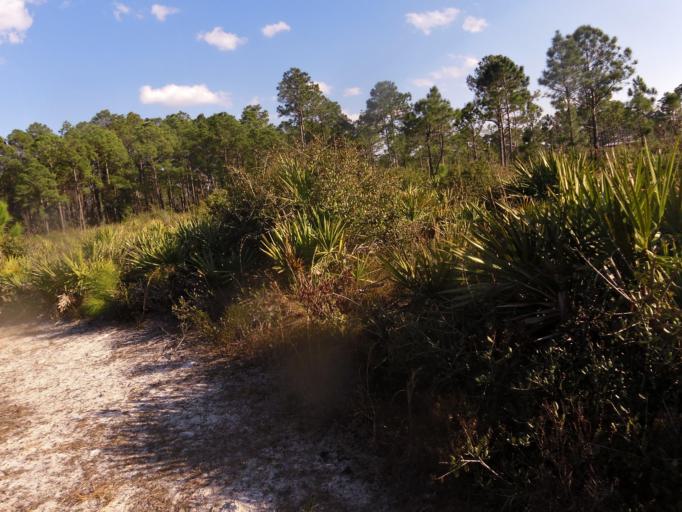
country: US
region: Florida
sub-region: Duval County
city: Atlantic Beach
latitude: 30.4747
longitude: -81.4881
